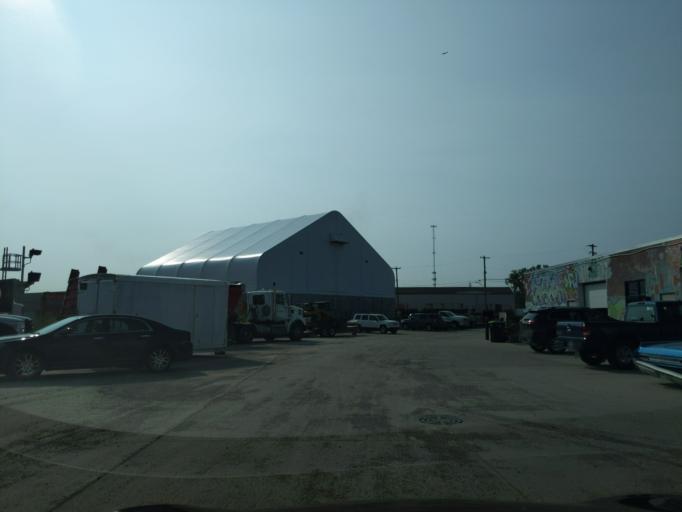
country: US
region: Michigan
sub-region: Ingham County
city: Lansing
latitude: 42.7195
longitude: -84.5418
